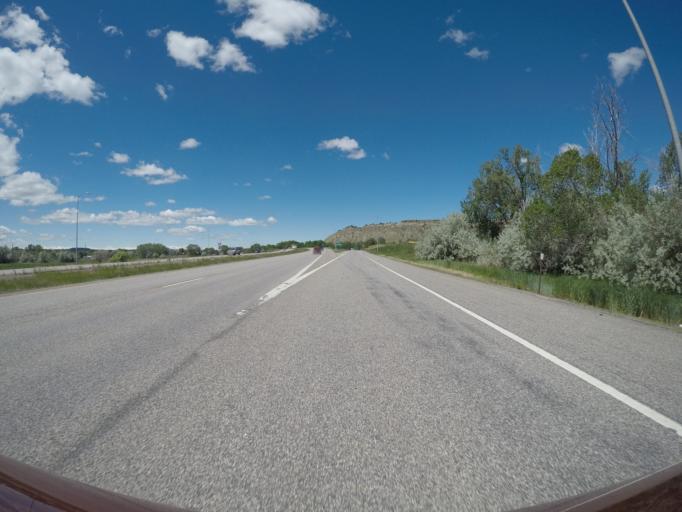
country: US
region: Montana
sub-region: Yellowstone County
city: Laurel
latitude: 45.6363
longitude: -108.9094
